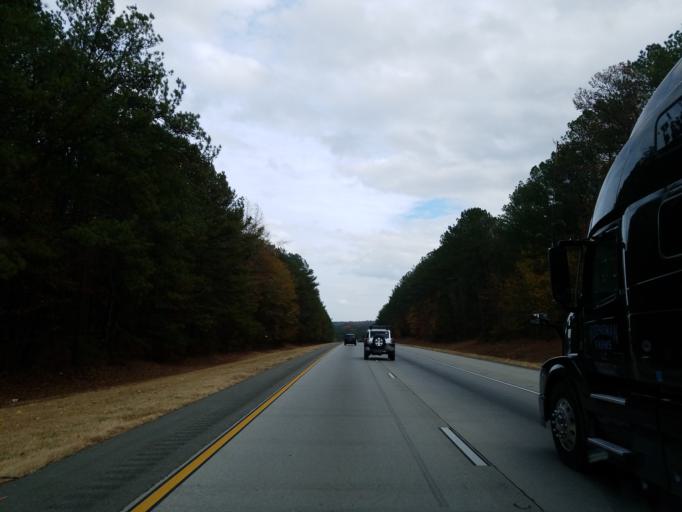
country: US
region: Georgia
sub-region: Carroll County
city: Mount Zion
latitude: 33.6872
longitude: -85.2382
